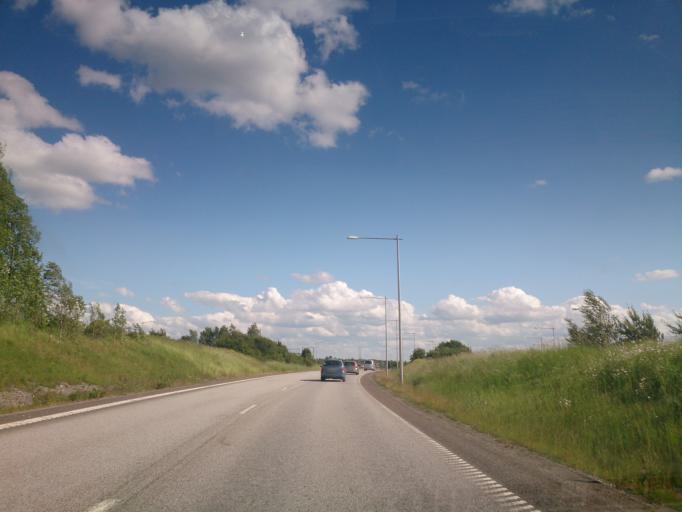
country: SE
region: OEstergoetland
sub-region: Norrkopings Kommun
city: Jursla
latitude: 58.6313
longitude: 16.1568
